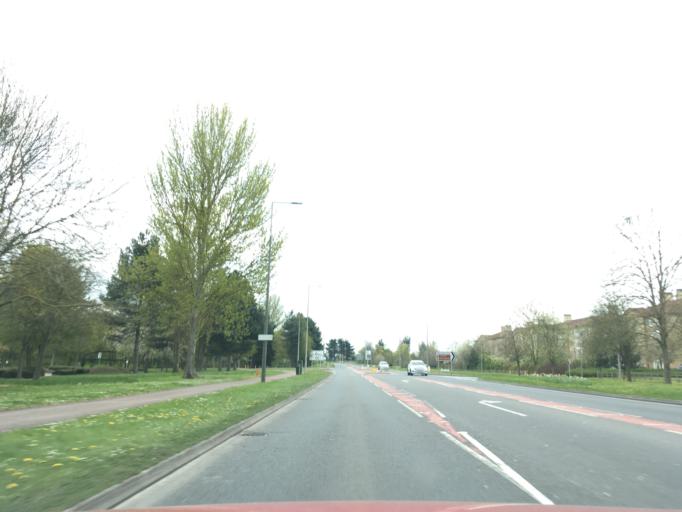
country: GB
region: England
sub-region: Milton Keynes
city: Newport Pagnell
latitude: 52.0572
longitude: -0.7288
